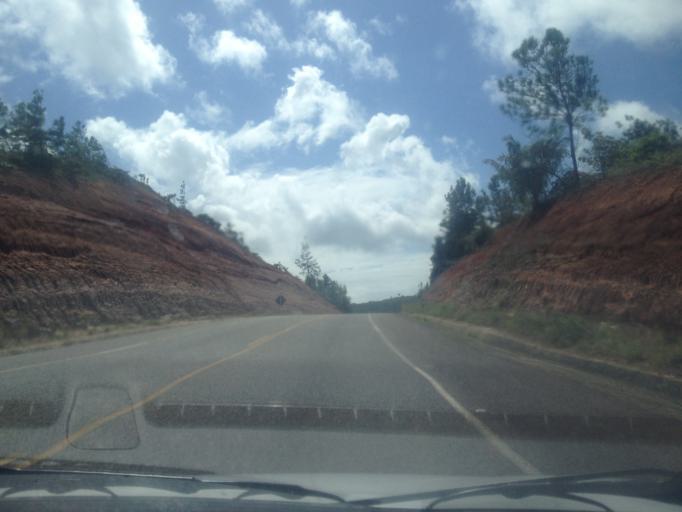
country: BR
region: Bahia
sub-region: Conde
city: Conde
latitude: -11.9835
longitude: -37.6771
